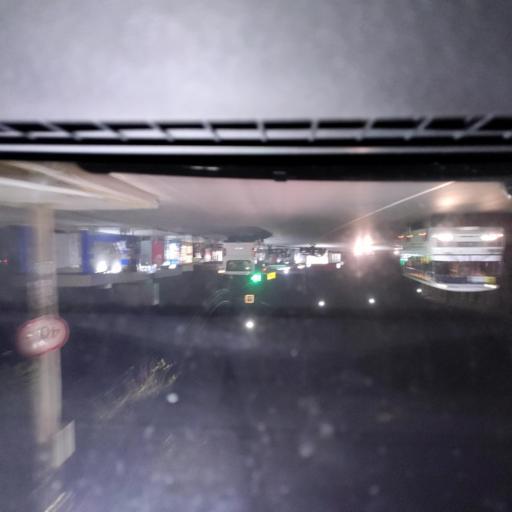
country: RU
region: Voronezj
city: Voronezh
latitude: 51.7245
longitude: 39.2629
